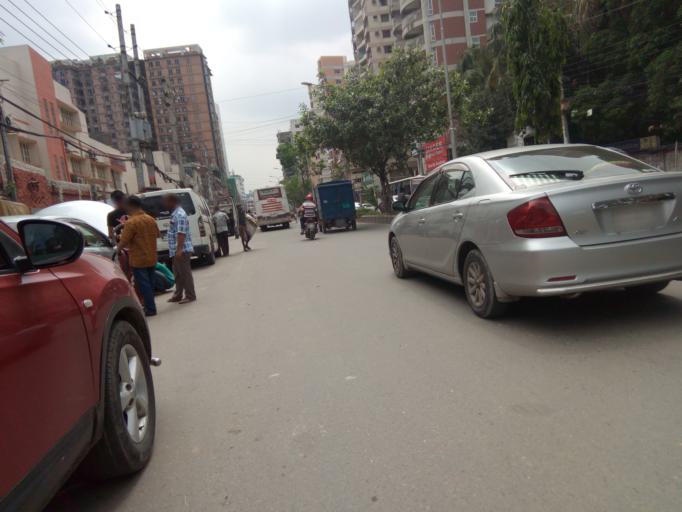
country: BD
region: Dhaka
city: Paltan
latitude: 23.7468
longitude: 90.3980
